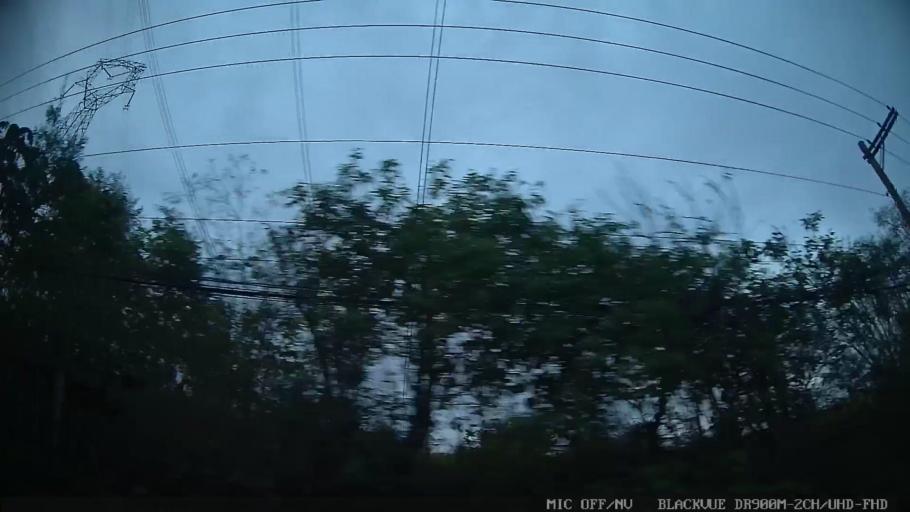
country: BR
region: Sao Paulo
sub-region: Louveira
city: Louveira
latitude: -23.1218
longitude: -46.9639
